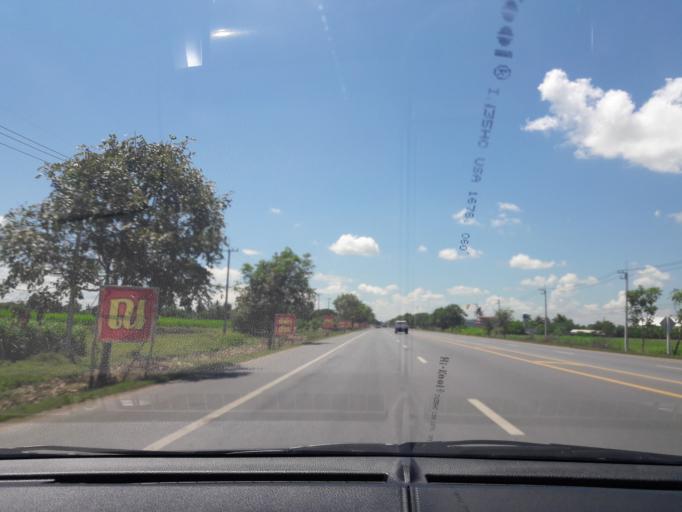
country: TH
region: Kanchanaburi
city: Tha Maka
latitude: 14.0321
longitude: 99.8289
